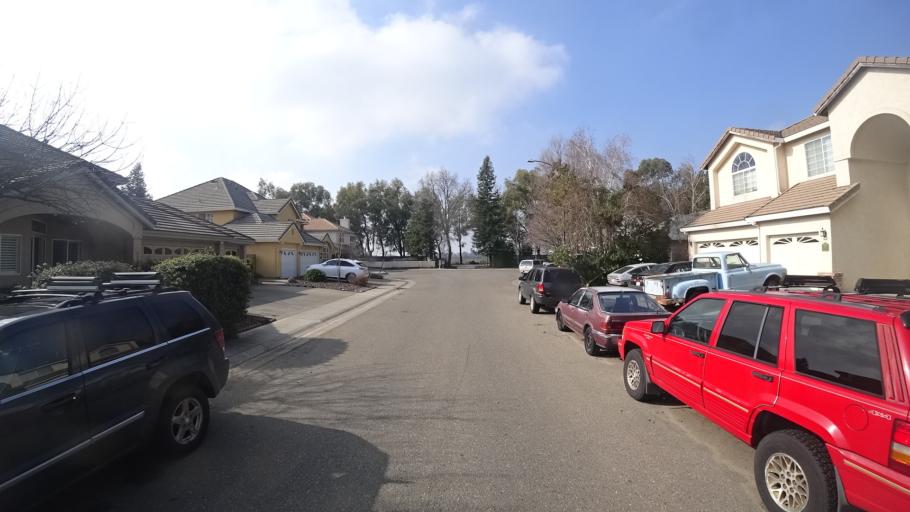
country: US
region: California
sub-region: Yolo County
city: Davis
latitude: 38.5740
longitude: -121.7570
